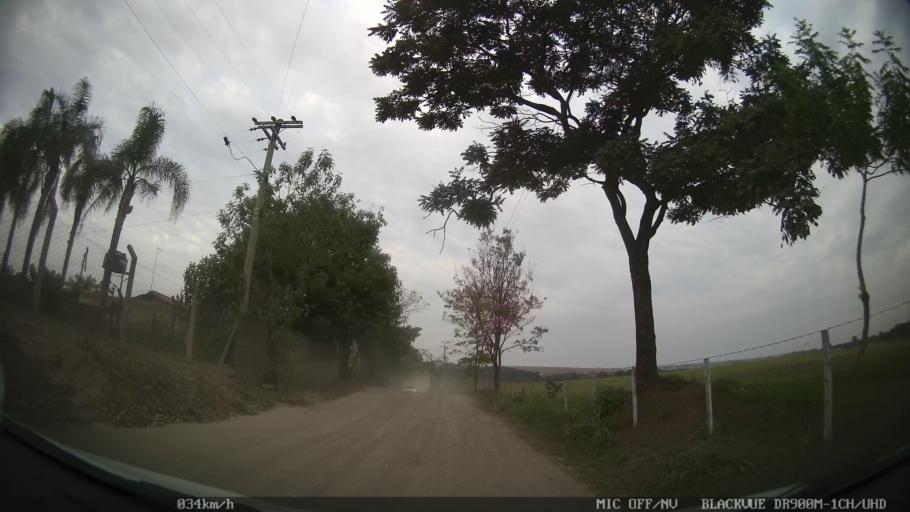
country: BR
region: Sao Paulo
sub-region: Santa Barbara D'Oeste
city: Santa Barbara d'Oeste
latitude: -22.6890
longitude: -47.3879
